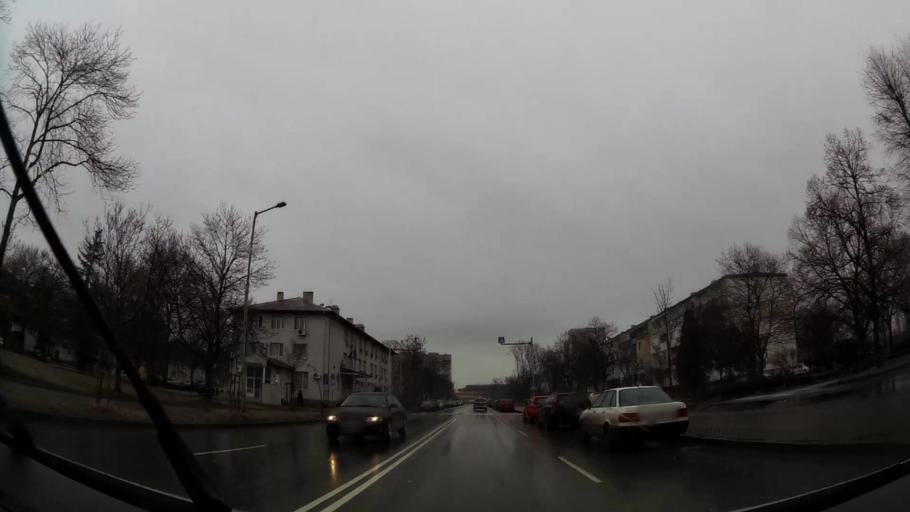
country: BG
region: Sofia-Capital
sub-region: Stolichna Obshtina
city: Sofia
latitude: 42.6659
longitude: 23.4002
